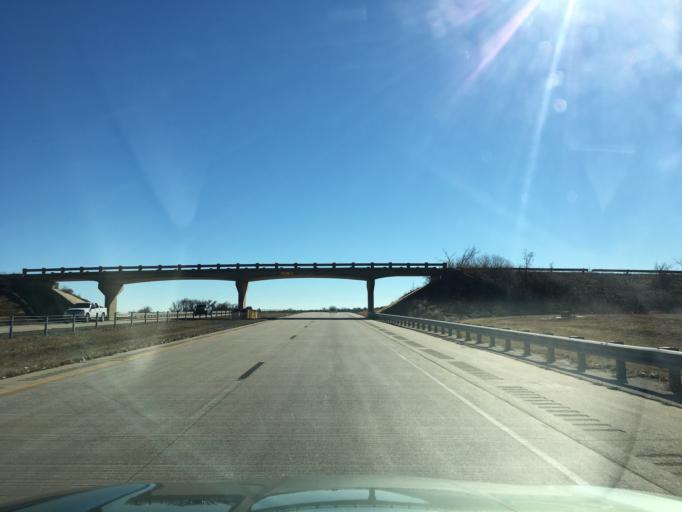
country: US
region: Oklahoma
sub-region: Kay County
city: Tonkawa
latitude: 36.4934
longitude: -97.3310
